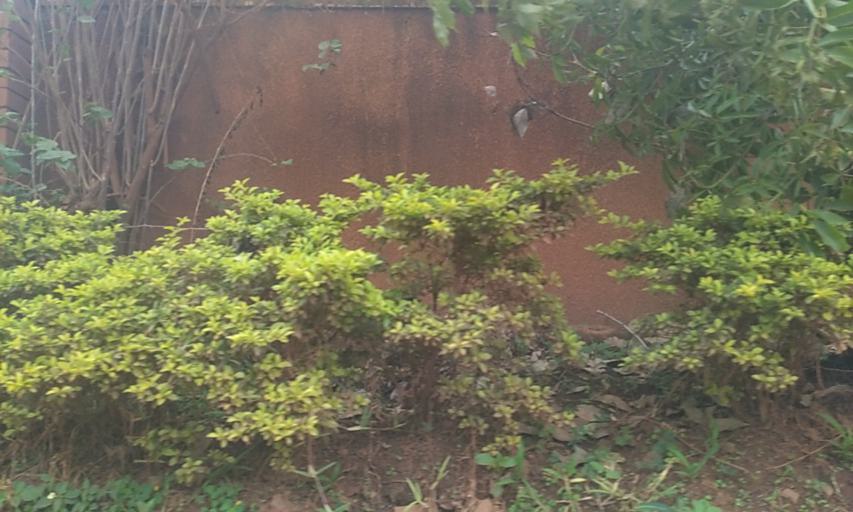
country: UG
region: Central Region
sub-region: Wakiso District
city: Kireka
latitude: 0.3436
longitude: 32.6211
